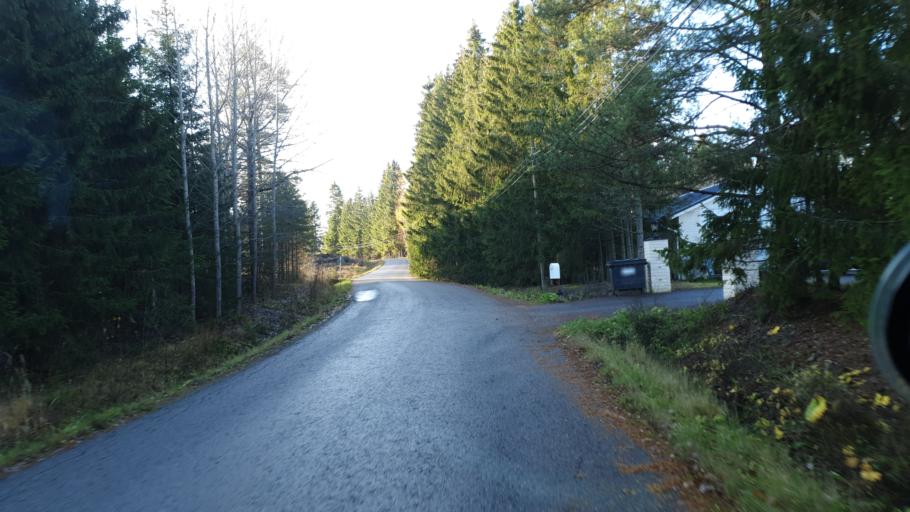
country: FI
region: Uusimaa
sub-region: Helsinki
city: Lohja
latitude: 60.2394
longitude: 24.1710
